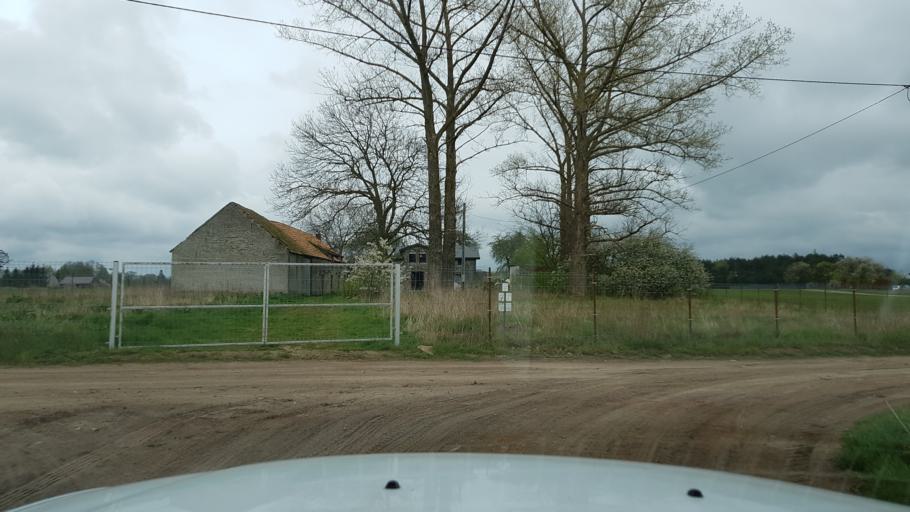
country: PL
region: West Pomeranian Voivodeship
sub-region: Powiat kolobrzeski
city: Ryman
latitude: 54.0338
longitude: 15.4789
